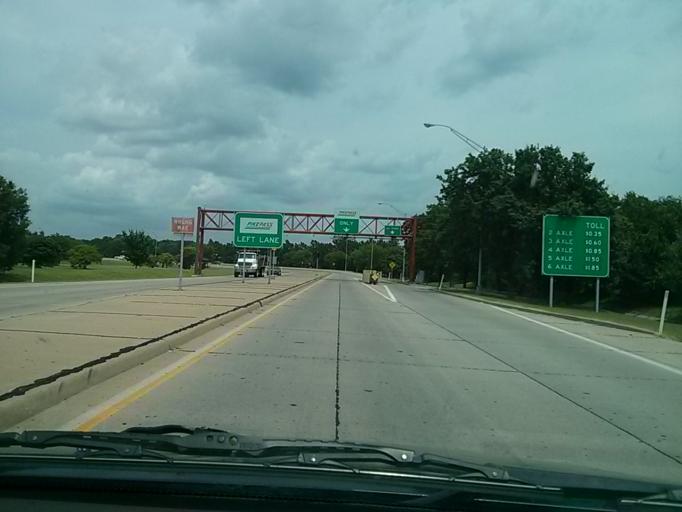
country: US
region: Oklahoma
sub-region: Tulsa County
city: Jenks
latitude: 36.0186
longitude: -95.9484
